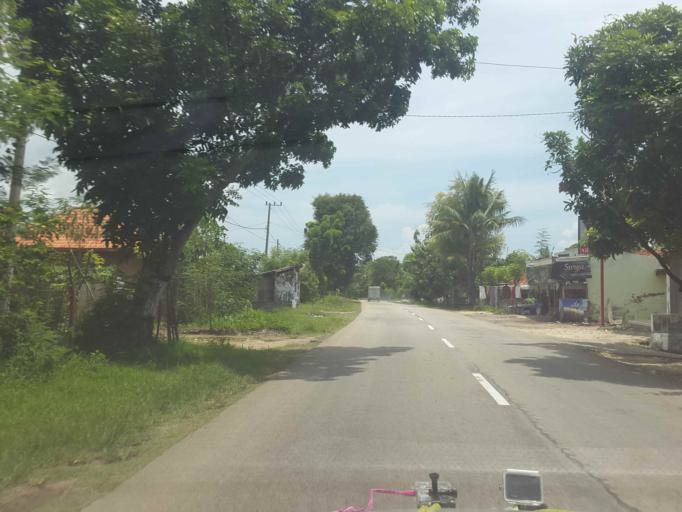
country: ID
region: East Java
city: Lobuk
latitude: -7.1218
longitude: 113.7875
